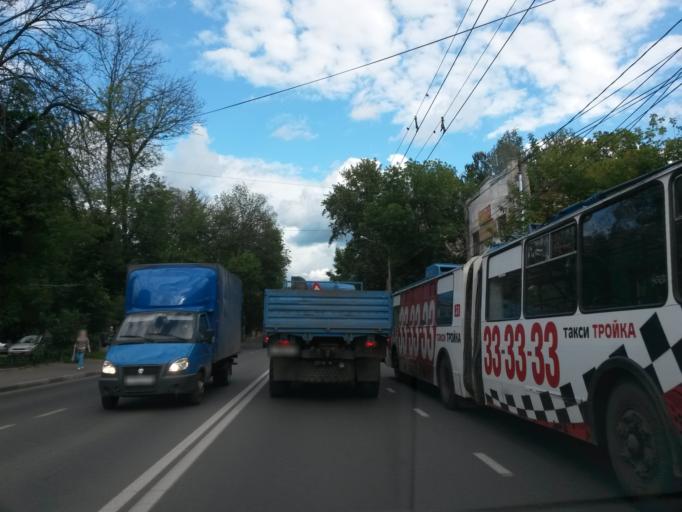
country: RU
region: Jaroslavl
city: Yaroslavl
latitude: 57.6344
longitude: 39.8738
